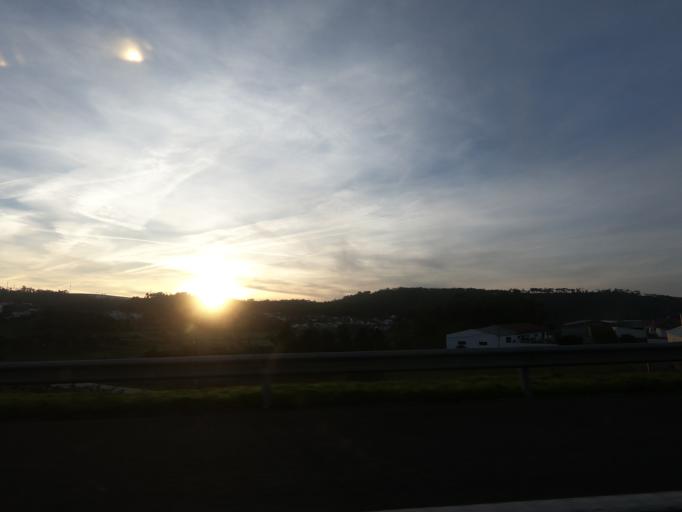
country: PT
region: Leiria
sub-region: Leiria
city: Caranguejeira
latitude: 39.7179
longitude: -8.7135
